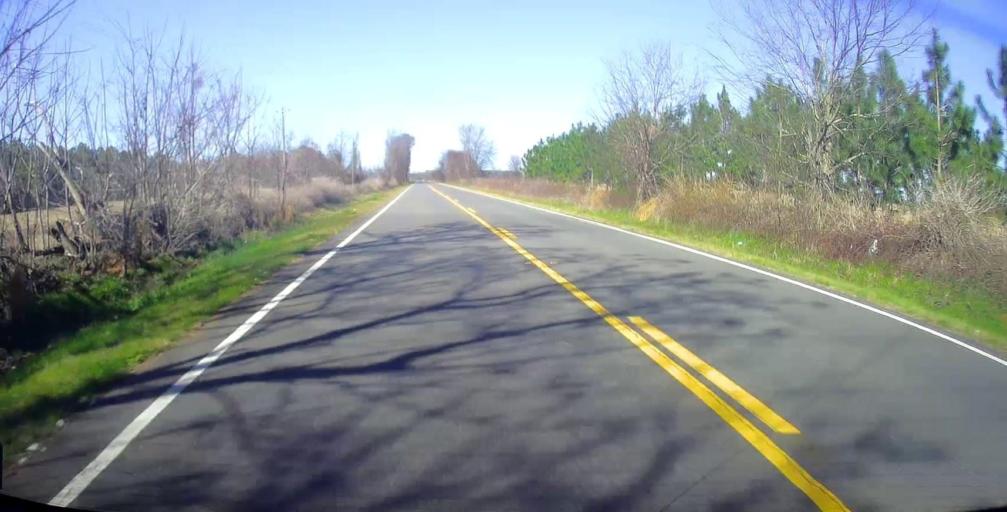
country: US
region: Georgia
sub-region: Macon County
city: Montezuma
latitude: 32.3782
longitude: -84.0148
